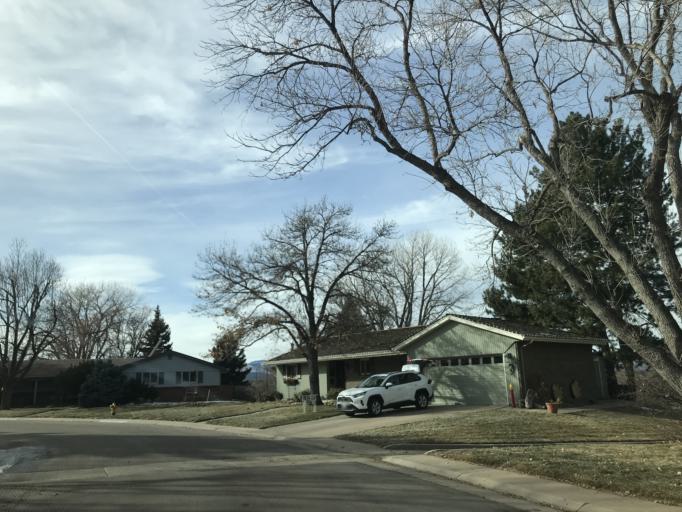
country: US
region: Colorado
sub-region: Arapahoe County
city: Columbine Valley
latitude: 39.5941
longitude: -105.0198
